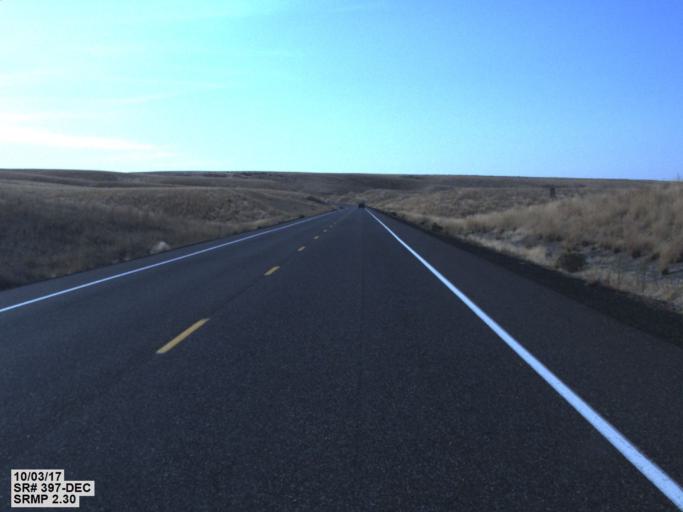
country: US
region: Washington
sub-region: Benton County
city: Highland
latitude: 46.1546
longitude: -119.1597
